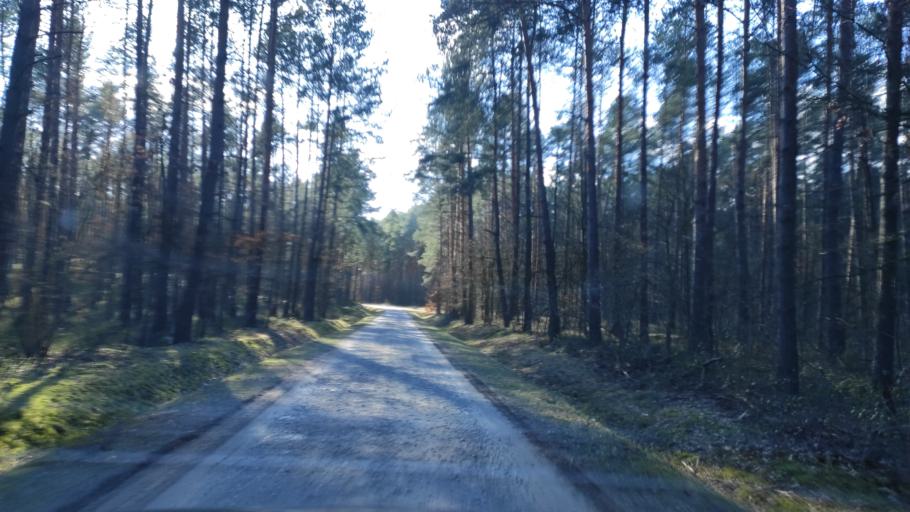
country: PL
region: Masovian Voivodeship
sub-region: Powiat radomski
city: Jastrzebia
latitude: 51.4686
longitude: 21.2368
